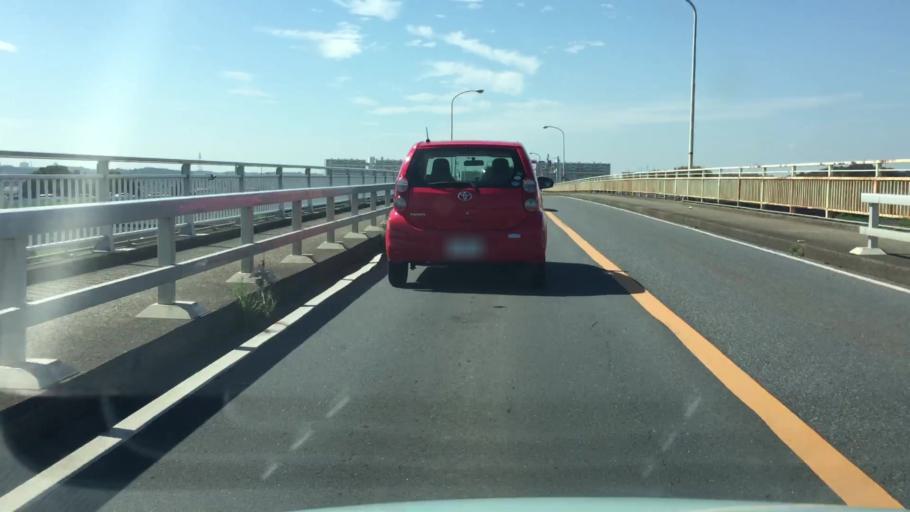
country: JP
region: Ibaraki
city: Ryugasaki
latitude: 35.8551
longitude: 140.1388
